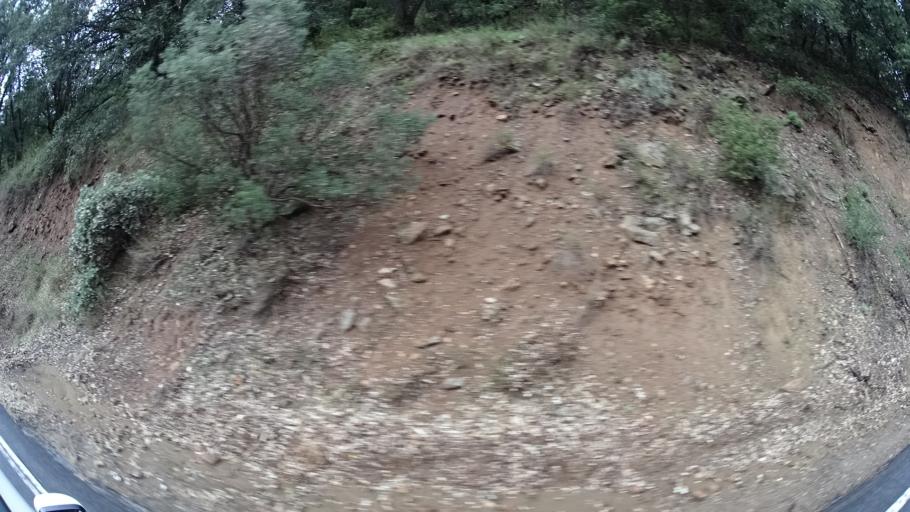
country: US
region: California
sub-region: San Diego County
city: Julian
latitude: 33.0965
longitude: -116.5905
